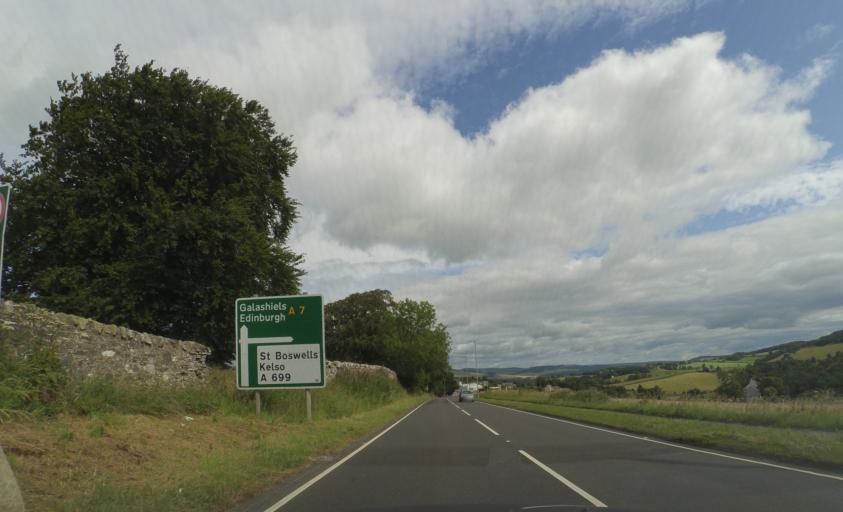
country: GB
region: Scotland
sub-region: The Scottish Borders
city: Selkirk
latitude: 55.5403
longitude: -2.8328
